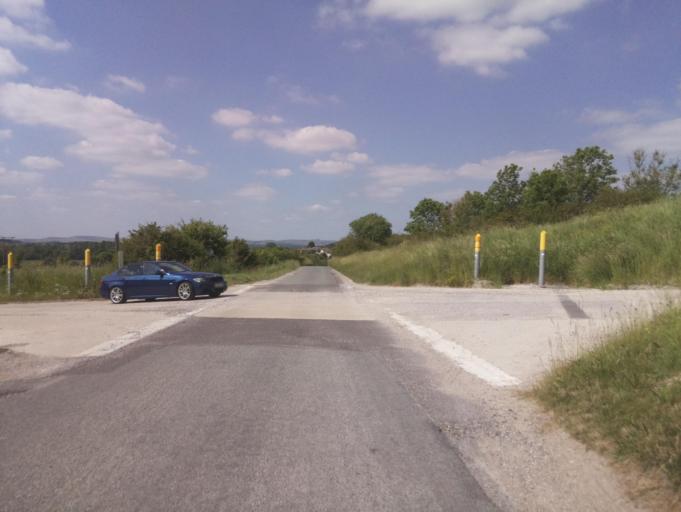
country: GB
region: England
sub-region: Wiltshire
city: Rushall
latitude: 51.2836
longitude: -1.8022
